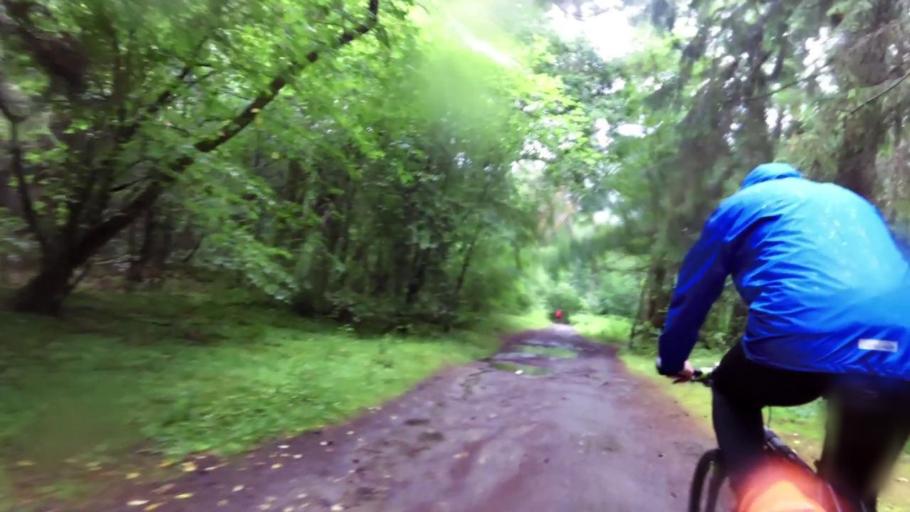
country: PL
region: West Pomeranian Voivodeship
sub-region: Powiat kolobrzeski
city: Ustronie Morskie
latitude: 54.2374
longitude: 15.8412
